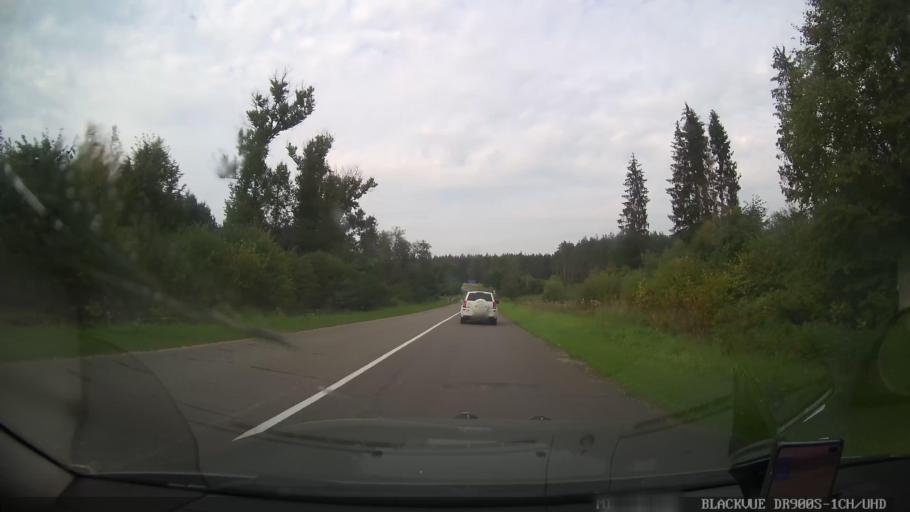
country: LT
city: Skaidiskes
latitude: 54.5889
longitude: 25.5565
